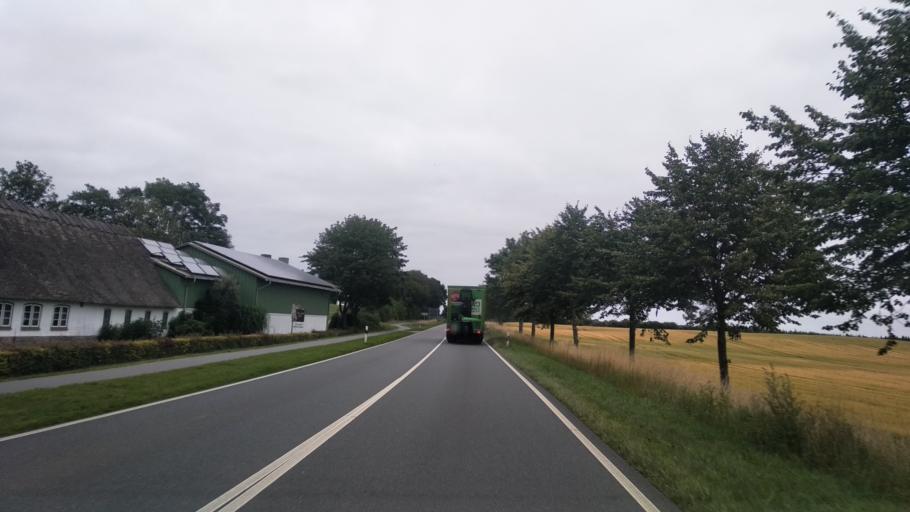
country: DE
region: Schleswig-Holstein
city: Wees
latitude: 54.8025
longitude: 9.5371
